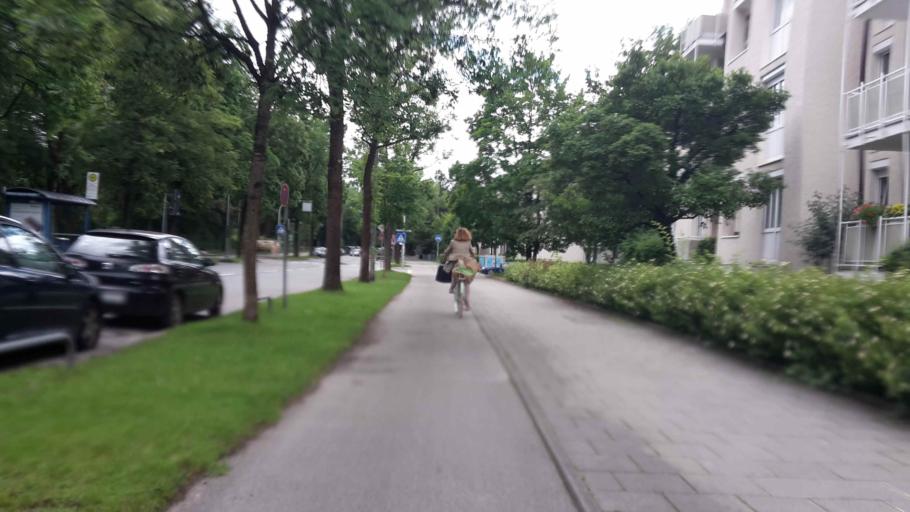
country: DE
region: Bavaria
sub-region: Upper Bavaria
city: Munich
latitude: 48.1045
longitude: 11.5620
